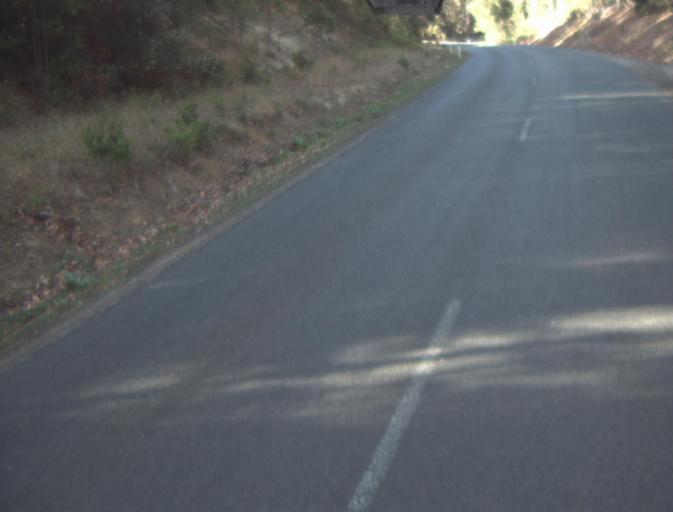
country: AU
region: Tasmania
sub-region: Launceston
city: Mayfield
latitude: -41.2144
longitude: 147.2115
